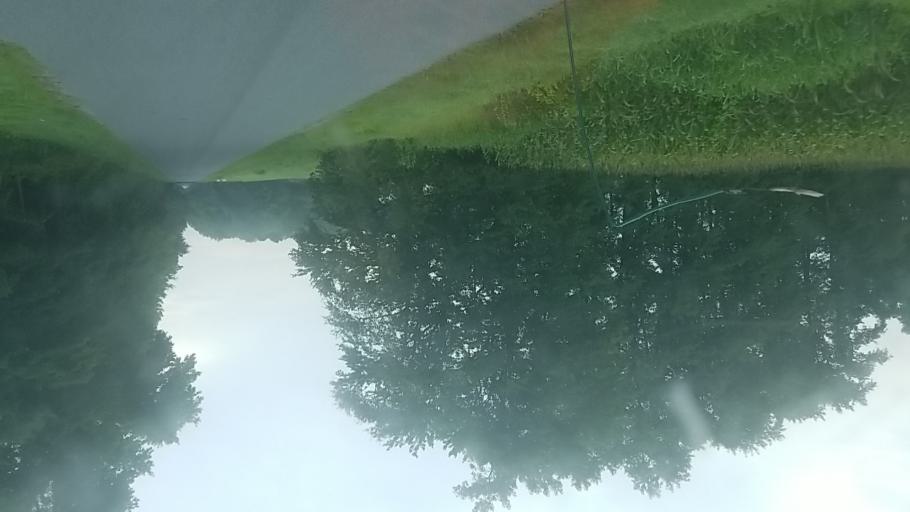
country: US
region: Maryland
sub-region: Wicomico County
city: Pittsville
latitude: 38.4521
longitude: -75.3904
